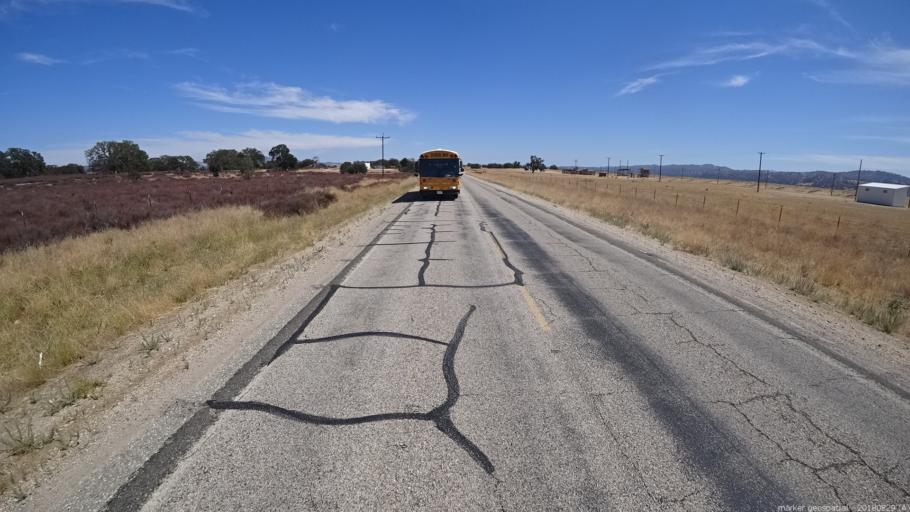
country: US
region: California
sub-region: Monterey County
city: King City
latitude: 35.9625
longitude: -121.1657
